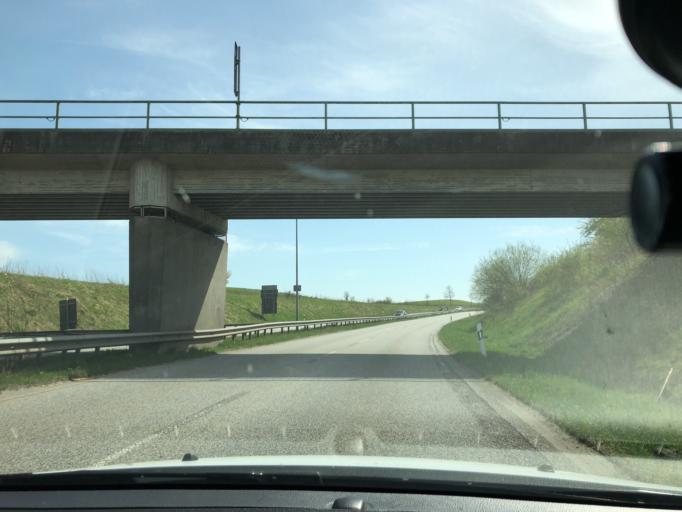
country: DE
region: Schleswig-Holstein
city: Tastrup
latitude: 54.7701
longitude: 9.4605
